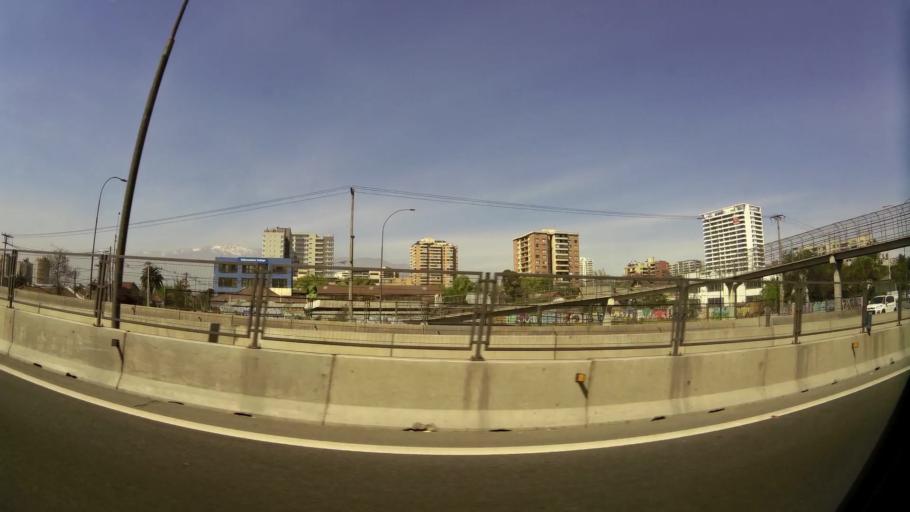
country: CL
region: Santiago Metropolitan
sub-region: Provincia de Santiago
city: Santiago
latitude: -33.4802
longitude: -70.6567
